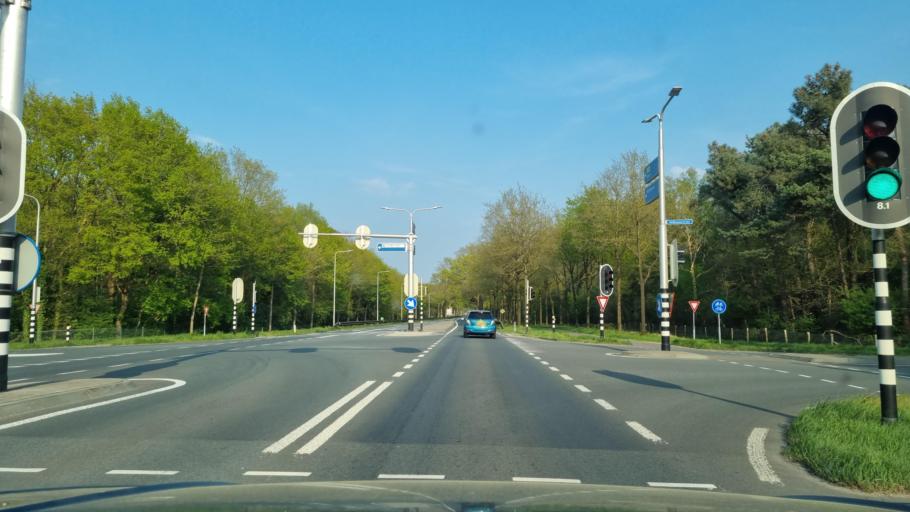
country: NL
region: North Brabant
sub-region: Gemeente Landerd
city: Schaijk
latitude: 51.7371
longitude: 5.6493
